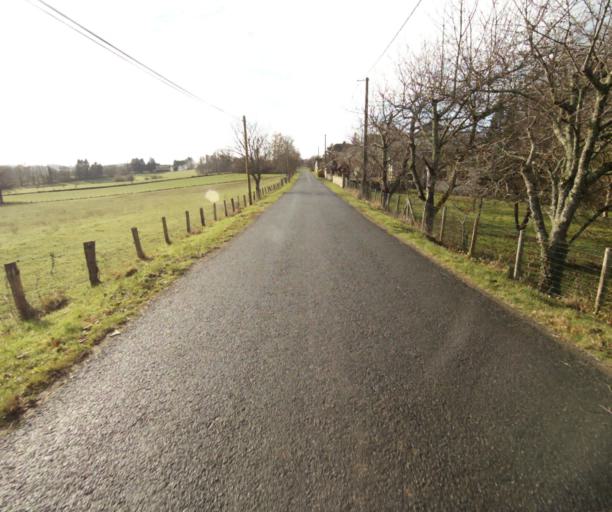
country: FR
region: Limousin
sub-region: Departement de la Correze
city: Saint-Mexant
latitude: 45.2755
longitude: 1.6046
